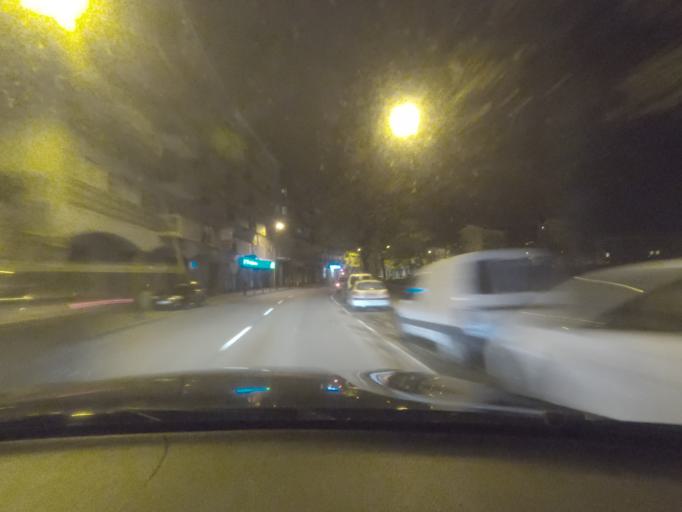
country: PT
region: Vila Real
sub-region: Vila Real
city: Vila Real
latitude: 41.2964
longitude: -7.7439
